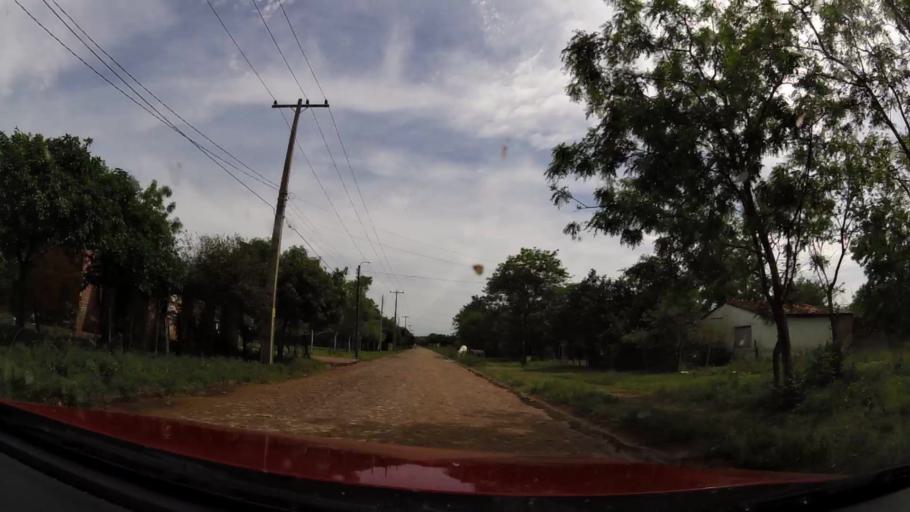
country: PY
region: Central
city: Limpio
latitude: -25.1865
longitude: -57.4737
